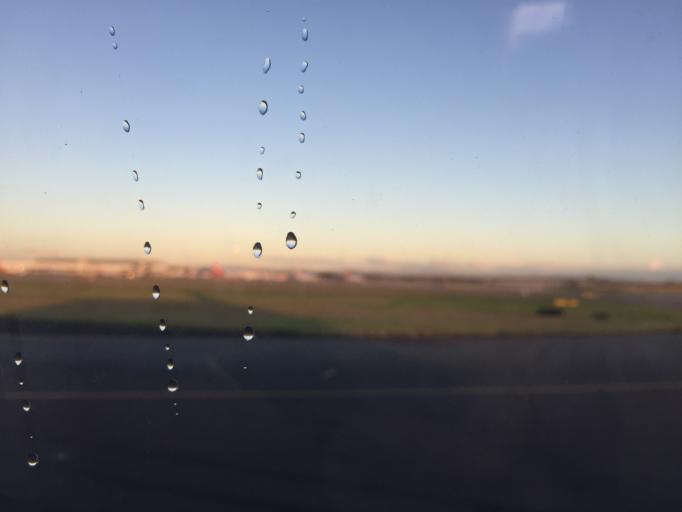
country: AU
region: Queensland
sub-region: Brisbane
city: Wynnum
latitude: -27.3814
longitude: 153.1306
